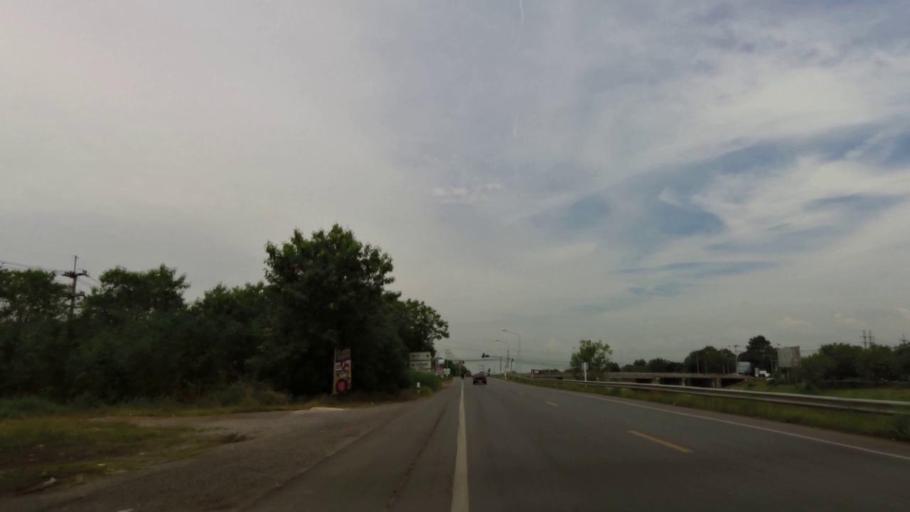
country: TH
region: Lop Buri
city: Ban Mi
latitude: 15.0460
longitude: 100.5637
